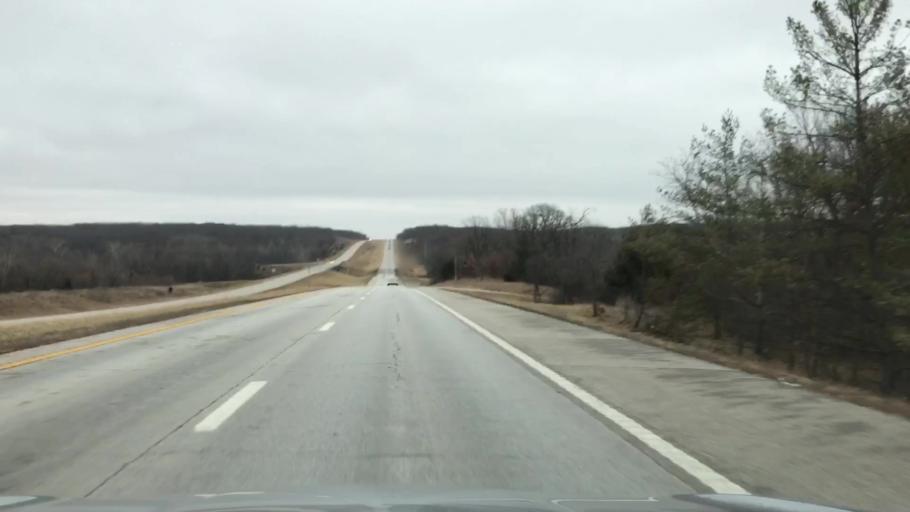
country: US
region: Missouri
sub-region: Linn County
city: Marceline
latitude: 39.7590
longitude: -92.8617
